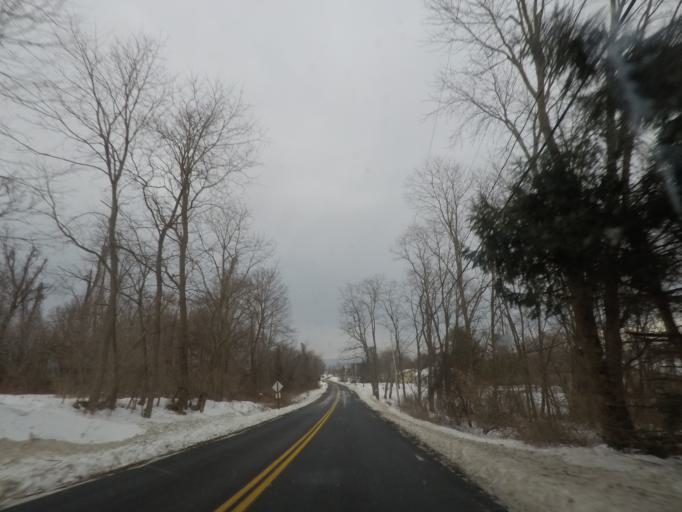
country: US
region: New York
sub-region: Rensselaer County
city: Castleton-on-Hudson
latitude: 42.5123
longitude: -73.7145
